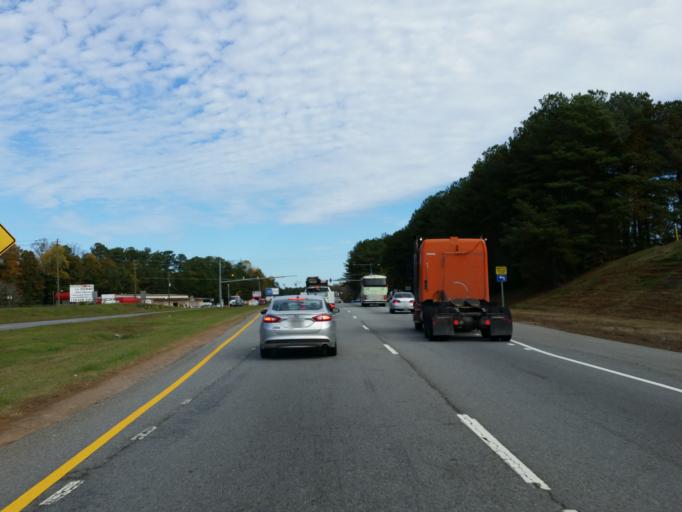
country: US
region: Georgia
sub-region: Cobb County
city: Marietta
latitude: 33.9970
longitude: -84.5308
